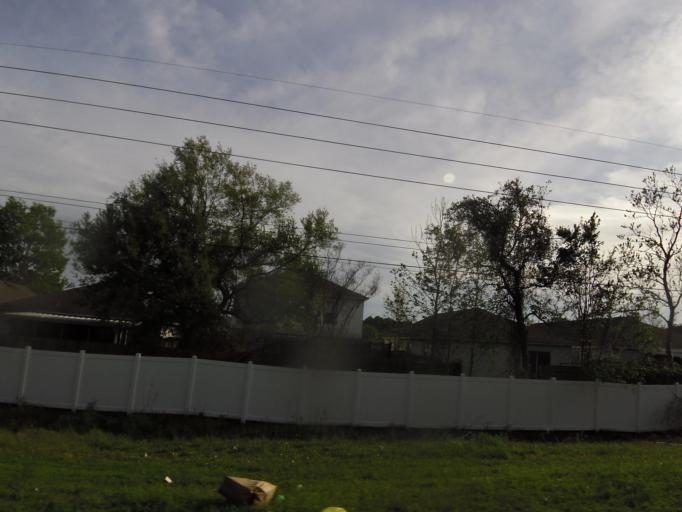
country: US
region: Florida
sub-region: Clay County
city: Bellair-Meadowbrook Terrace
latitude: 30.2260
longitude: -81.7610
